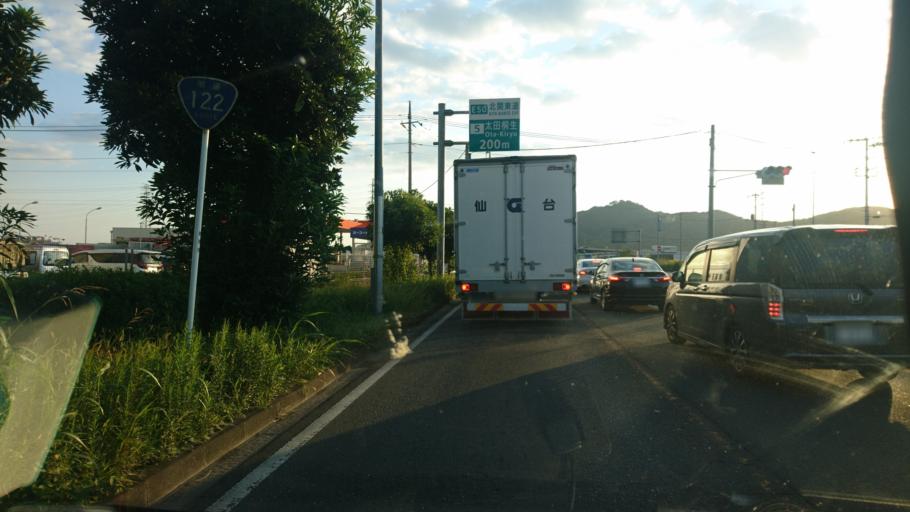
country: JP
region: Gunma
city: Ota
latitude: 36.3298
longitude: 139.3937
